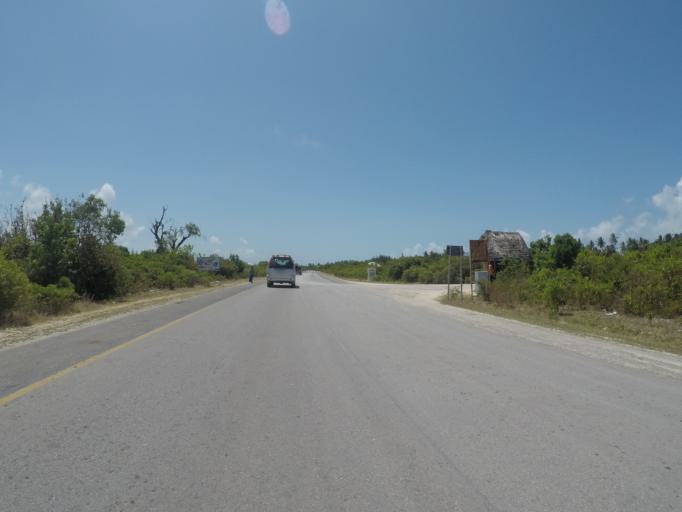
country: TZ
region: Zanzibar Central/South
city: Nganane
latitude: -6.3164
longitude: 39.5422
